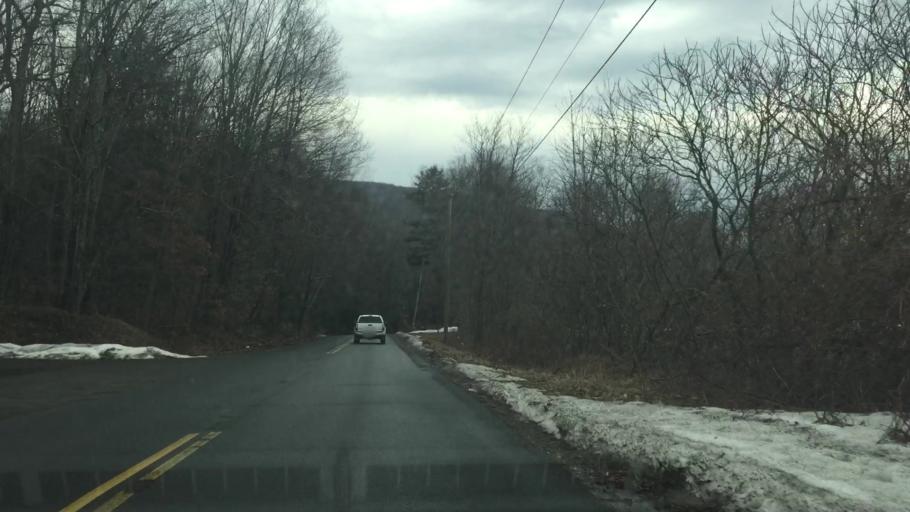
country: US
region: Massachusetts
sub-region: Hampshire County
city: Westhampton
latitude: 42.2099
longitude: -72.8475
